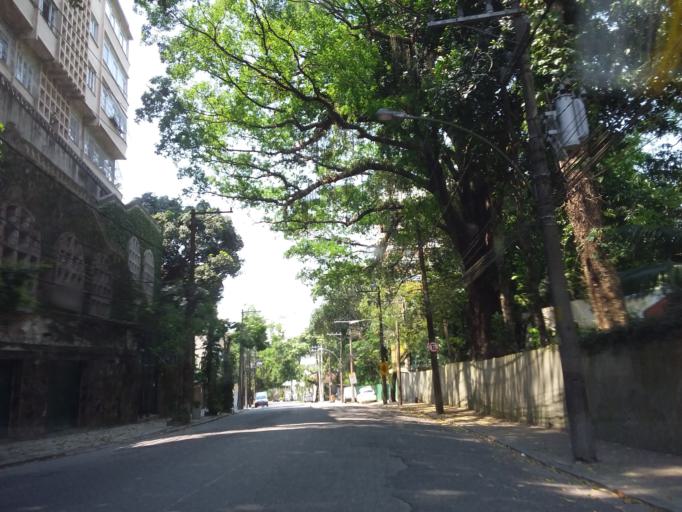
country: BR
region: Rio de Janeiro
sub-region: Rio De Janeiro
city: Rio de Janeiro
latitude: -22.9819
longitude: -43.2371
